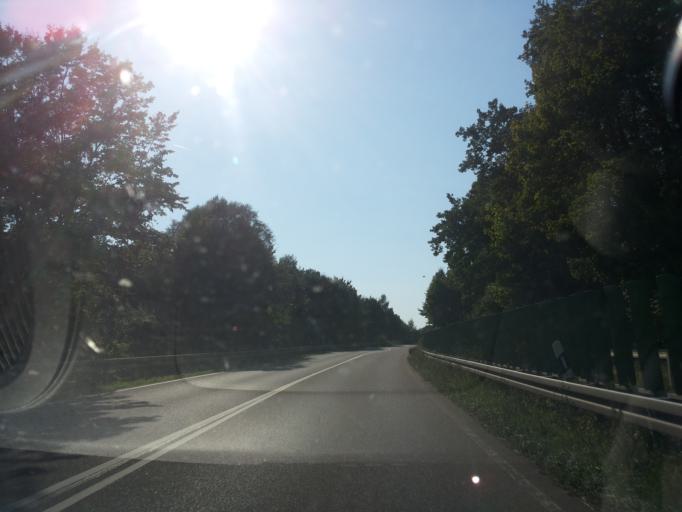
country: DE
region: Bavaria
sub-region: Upper Bavaria
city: Vohburg an der Donau
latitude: 48.7747
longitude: 11.6323
